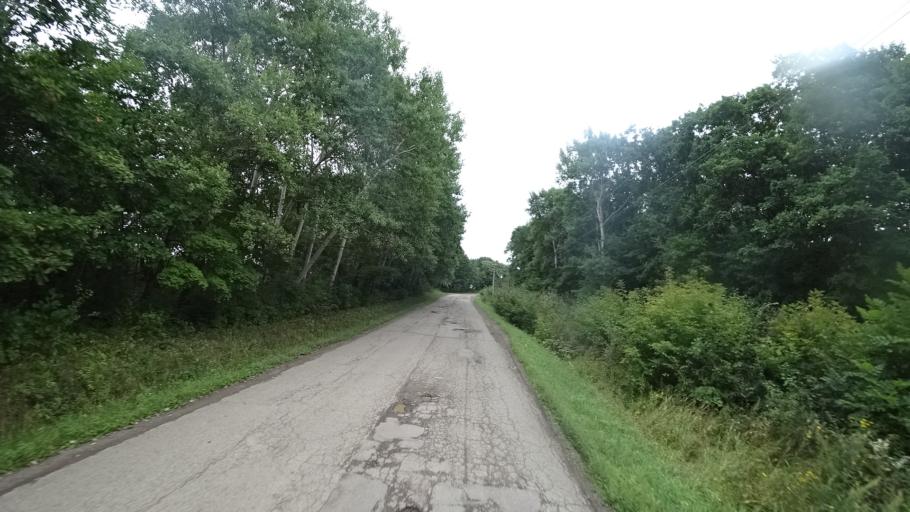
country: RU
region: Primorskiy
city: Chernigovka
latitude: 44.4548
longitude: 132.5955
